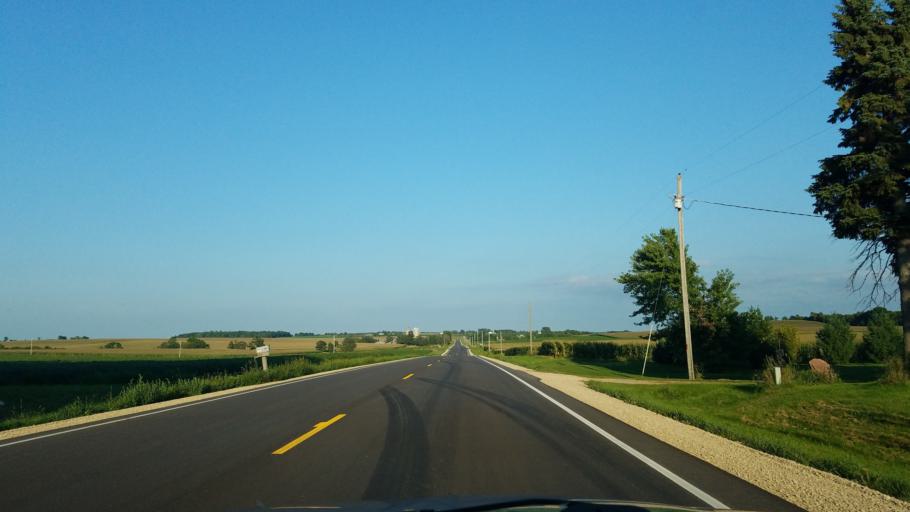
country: US
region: Wisconsin
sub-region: Saint Croix County
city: Hammond
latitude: 45.0791
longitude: -92.4003
